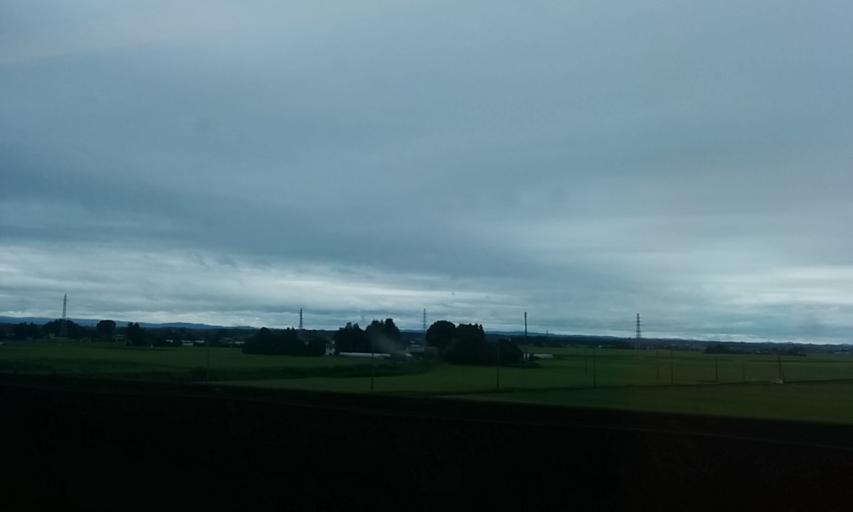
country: JP
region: Tochigi
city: Ujiie
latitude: 36.7097
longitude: 139.9226
